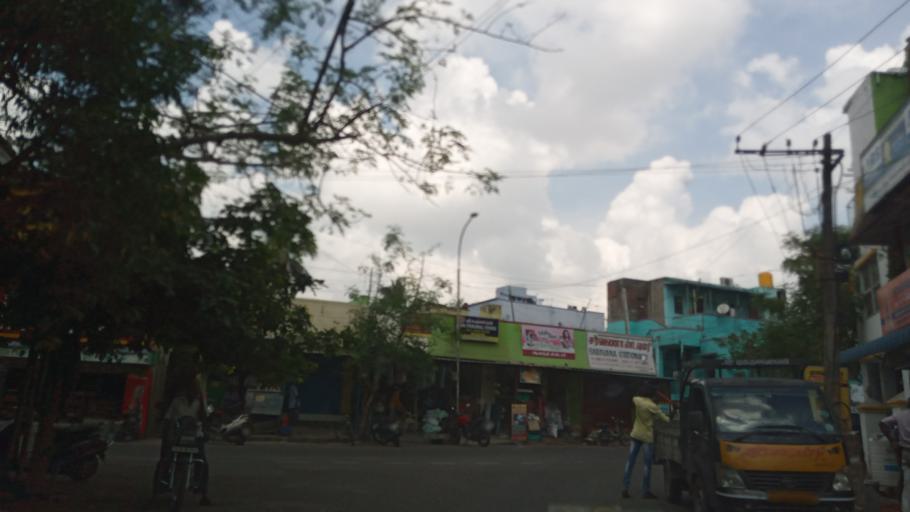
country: IN
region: Tamil Nadu
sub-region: Kancheepuram
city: Madipakkam
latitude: 12.9808
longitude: 80.1801
